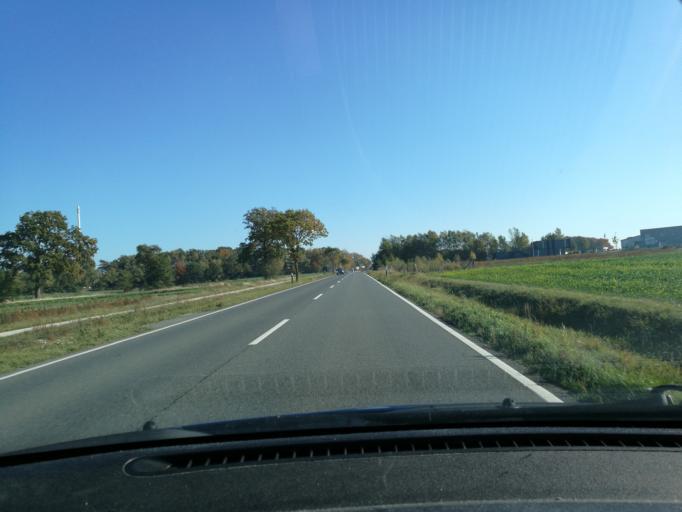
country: DE
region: Lower Saxony
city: Barendorf
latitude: 53.2097
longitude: 10.5256
